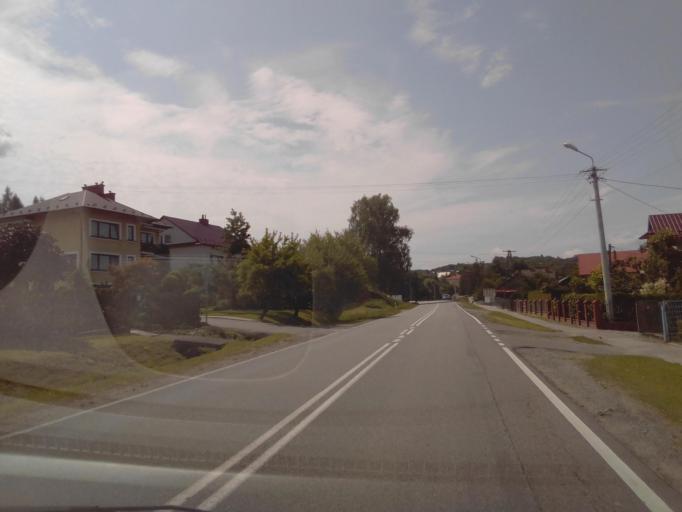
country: PL
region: Subcarpathian Voivodeship
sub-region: Powiat ropczycko-sedziszowski
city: Ropczyce
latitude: 50.0336
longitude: 21.5754
